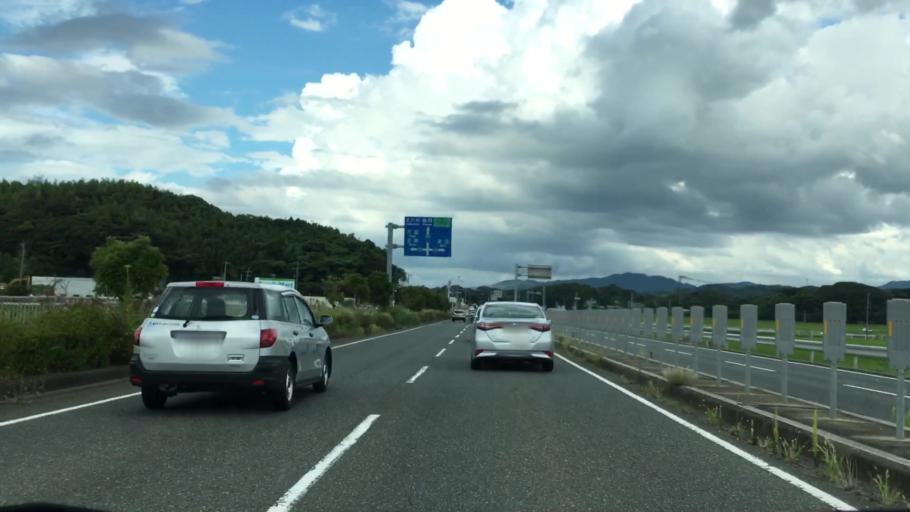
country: JP
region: Fukuoka
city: Maebaru-chuo
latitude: 33.5214
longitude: 130.1647
